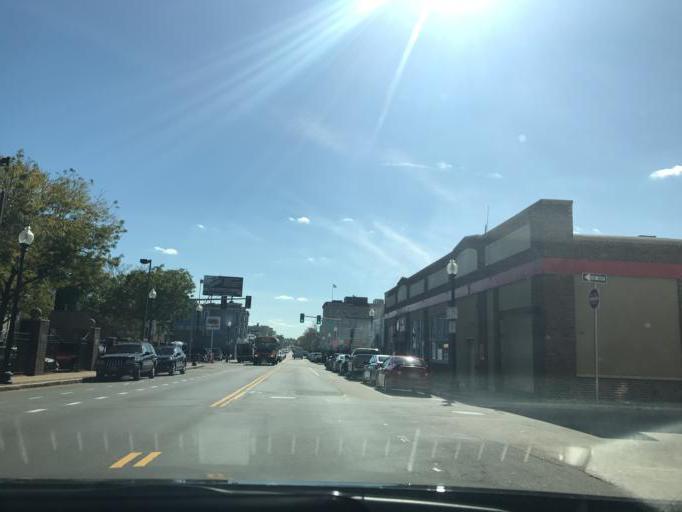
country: US
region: Massachusetts
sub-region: Suffolk County
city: South Boston
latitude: 42.3136
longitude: -71.0571
